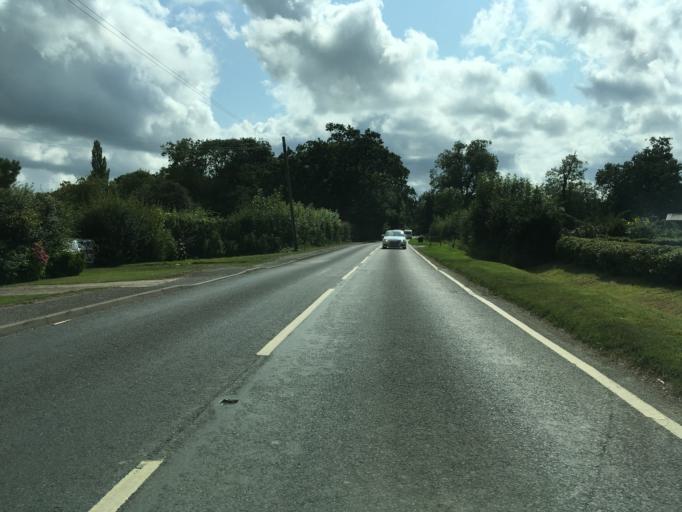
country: GB
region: England
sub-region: Kent
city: Headcorn
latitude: 51.1220
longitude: 0.6472
